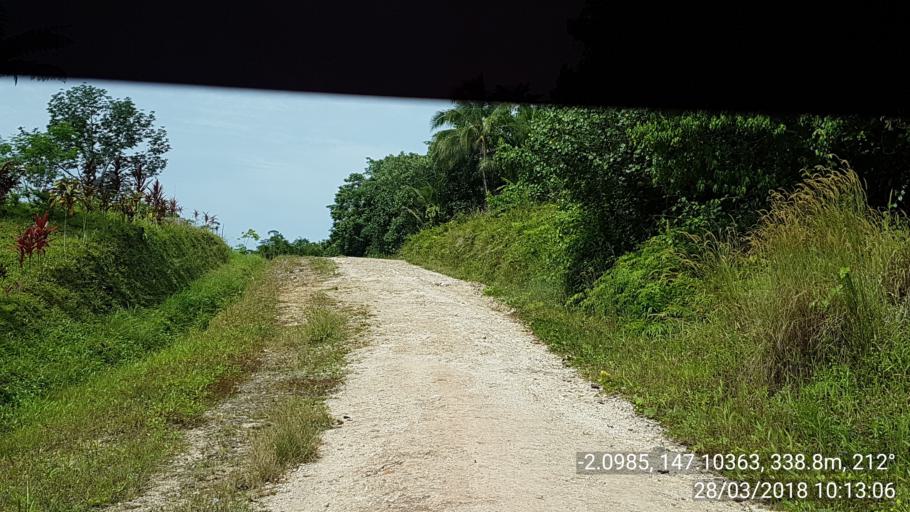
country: PG
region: Manus
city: Lorengau
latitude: -2.0986
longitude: 147.1036
